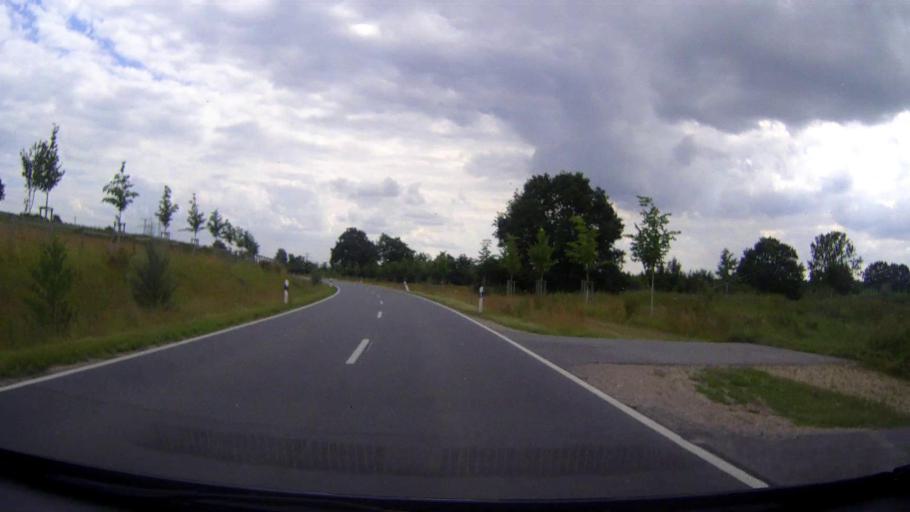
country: DE
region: Schleswig-Holstein
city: Badendorf
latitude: 53.8860
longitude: 10.6045
